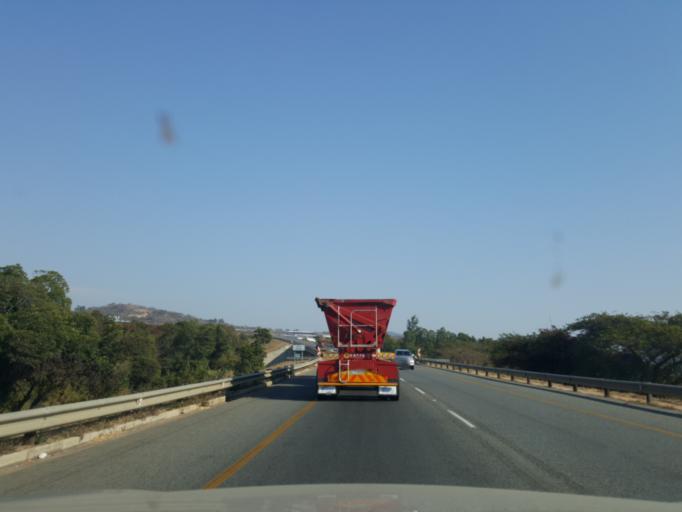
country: ZA
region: Mpumalanga
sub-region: Ehlanzeni District
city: Nelspruit
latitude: -25.4345
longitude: 30.9717
